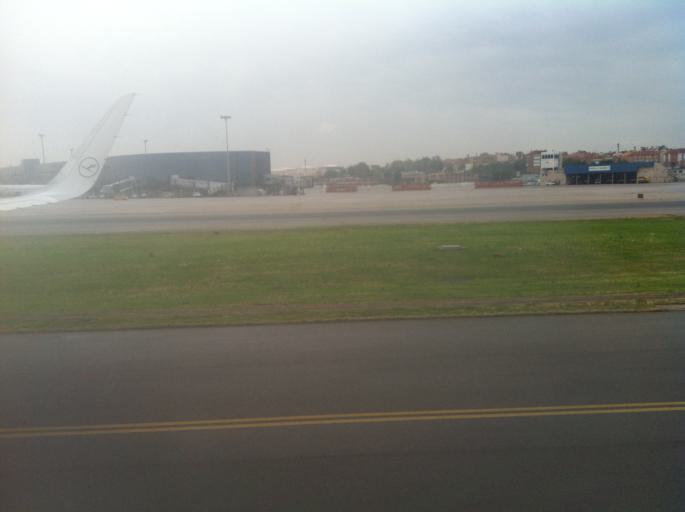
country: ES
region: Madrid
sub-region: Provincia de Madrid
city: Barajas de Madrid
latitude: 40.4749
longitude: -3.5685
